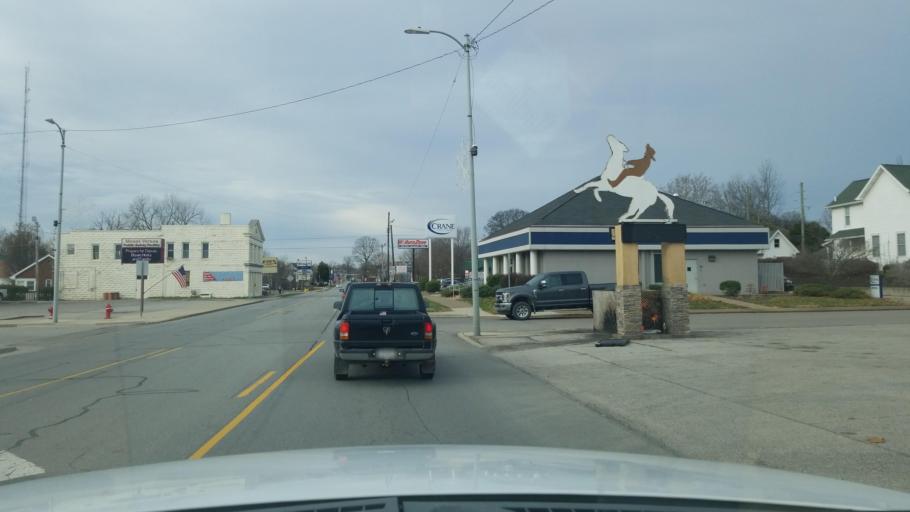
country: US
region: Indiana
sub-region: Posey County
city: Mount Vernon
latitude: 37.9320
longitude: -87.8966
